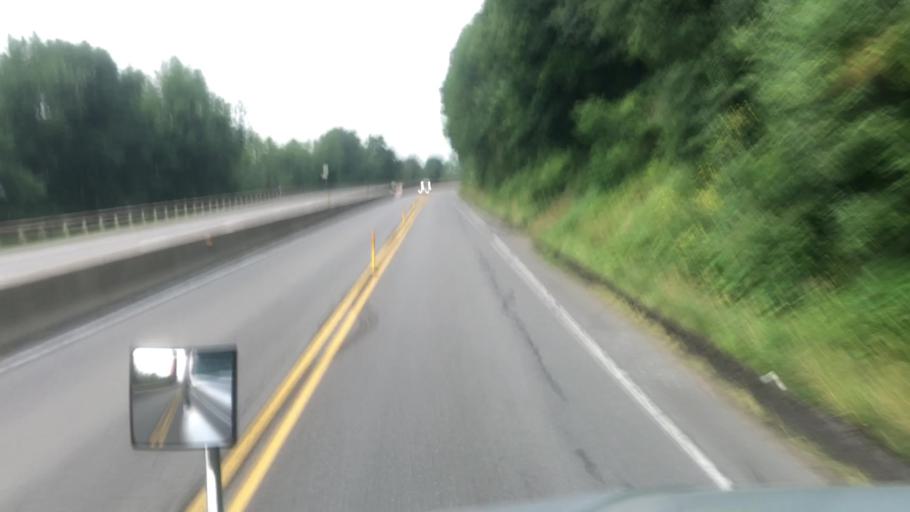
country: US
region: Pennsylvania
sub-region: Venango County
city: Woodland Heights
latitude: 41.4152
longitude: -79.7328
